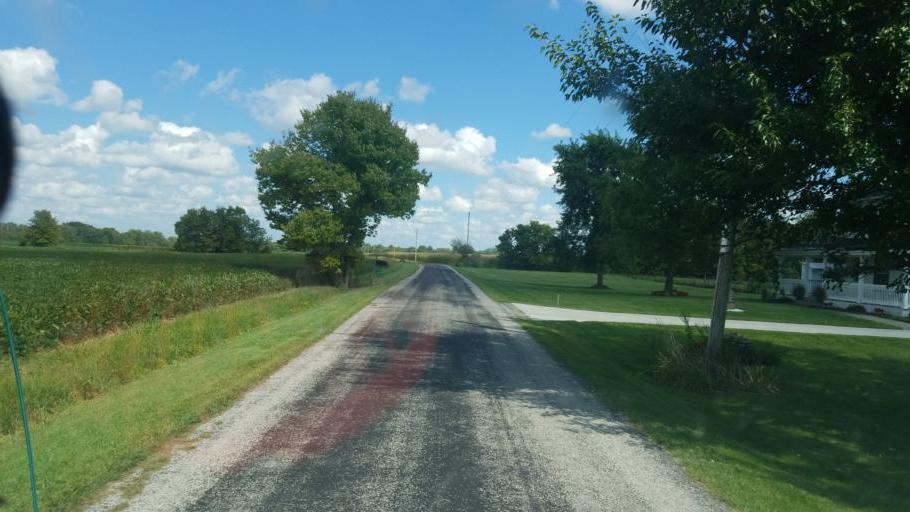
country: US
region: Ohio
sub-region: Marion County
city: Prospect
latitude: 40.3603
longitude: -83.2008
